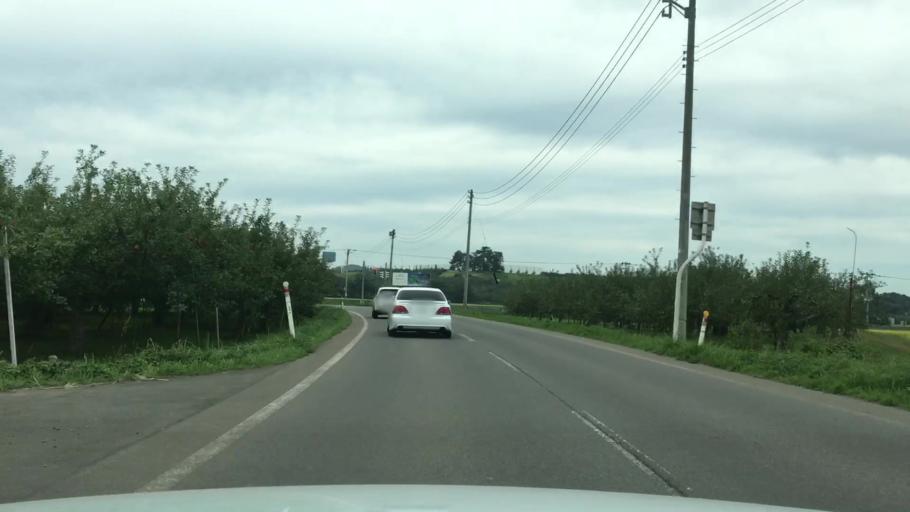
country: JP
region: Aomori
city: Hirosaki
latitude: 40.6582
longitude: 140.4192
